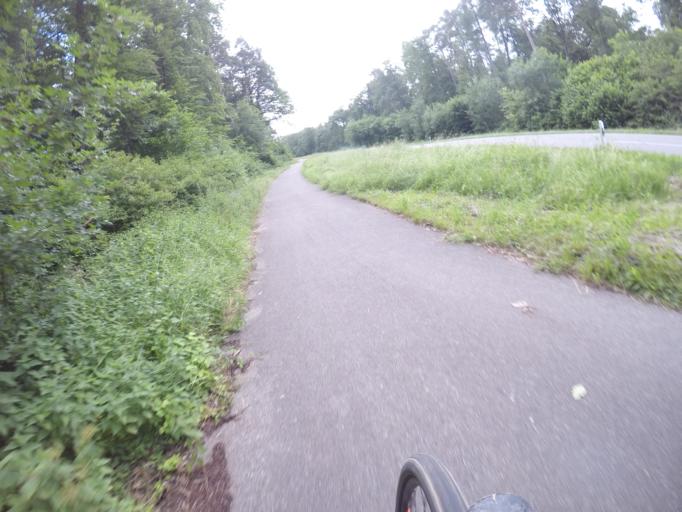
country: DE
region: Baden-Wuerttemberg
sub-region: Regierungsbezirk Stuttgart
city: Kohlberg
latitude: 48.5691
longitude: 9.3287
